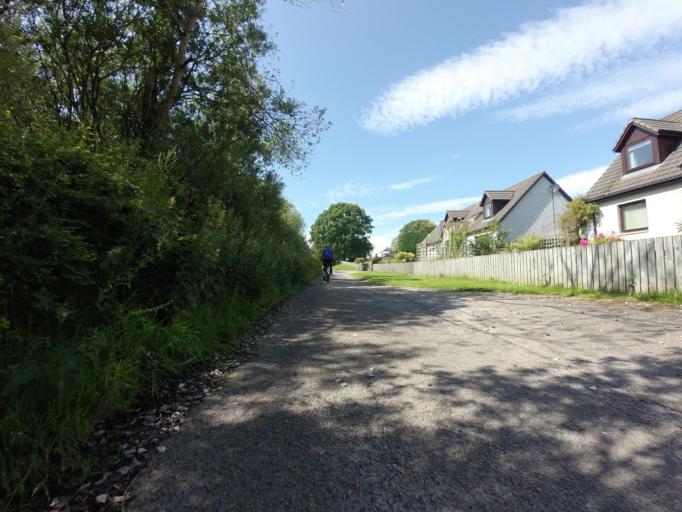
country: GB
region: Scotland
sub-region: Highland
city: Conon Bridge
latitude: 57.5407
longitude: -4.3417
